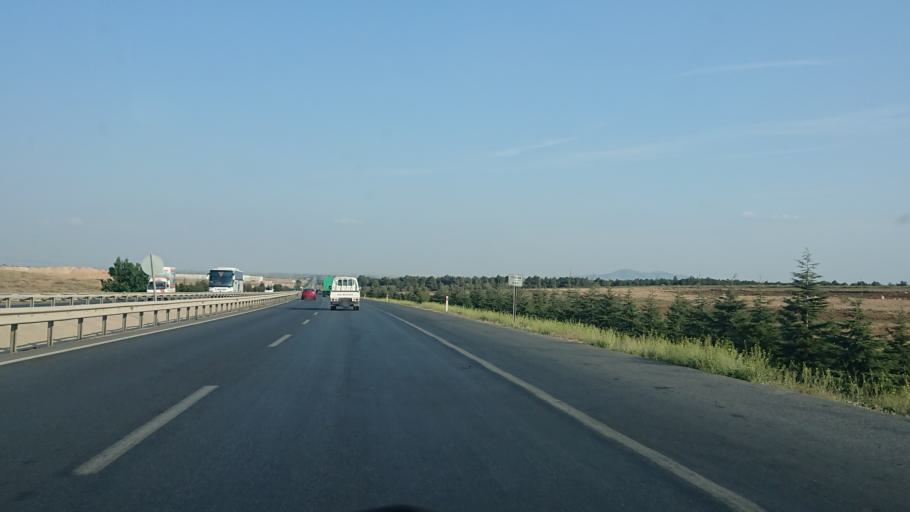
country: TR
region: Eskisehir
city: Sevinc
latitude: 39.7016
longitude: 30.7014
